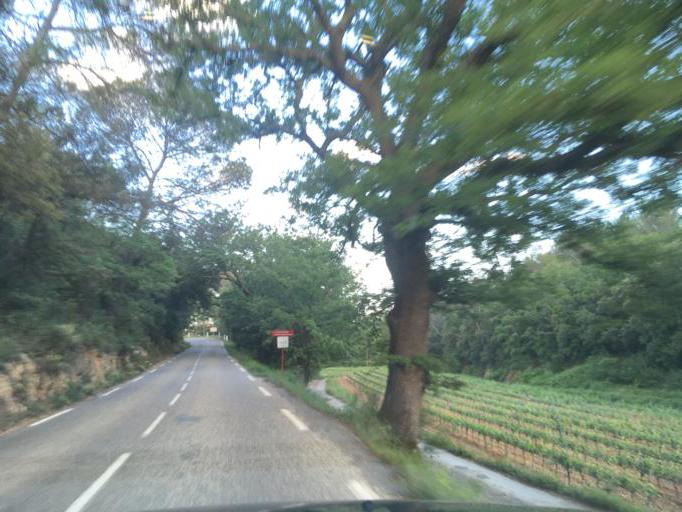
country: FR
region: Provence-Alpes-Cote d'Azur
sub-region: Departement du Var
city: Carces
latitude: 43.4940
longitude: 6.2179
